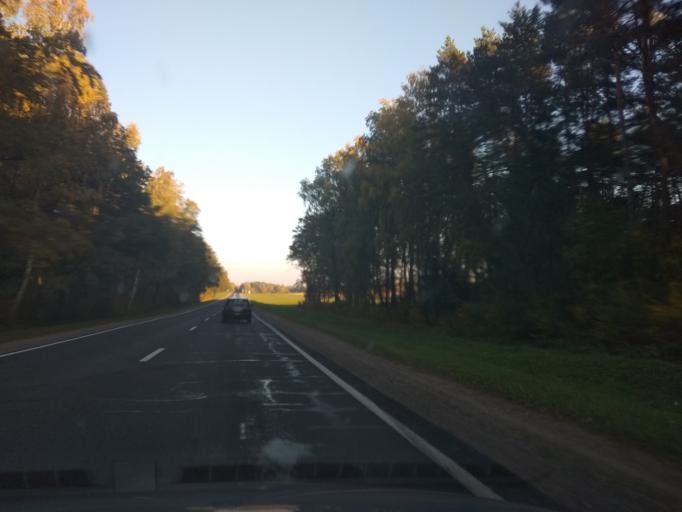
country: BY
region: Grodnenskaya
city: Zel'va
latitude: 53.1416
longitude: 24.6342
